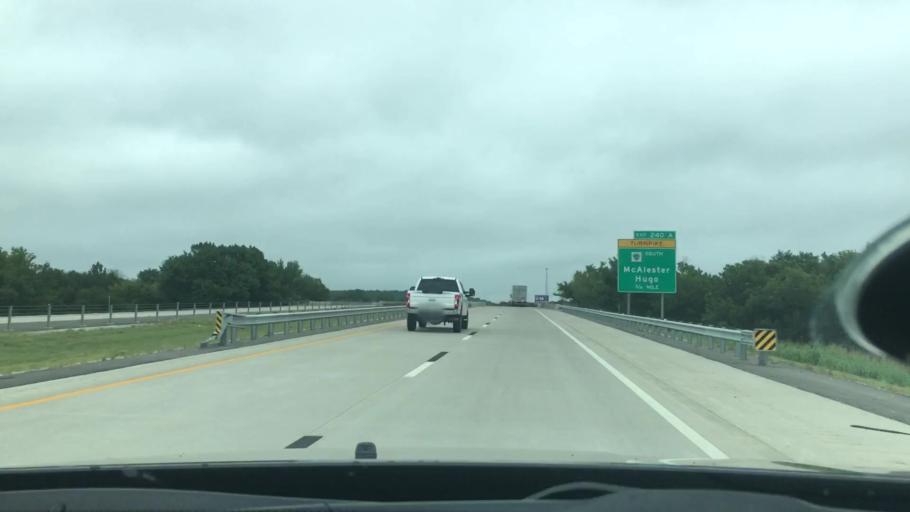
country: US
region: Oklahoma
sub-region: Okmulgee County
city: Henryetta
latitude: 35.4329
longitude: -95.9926
